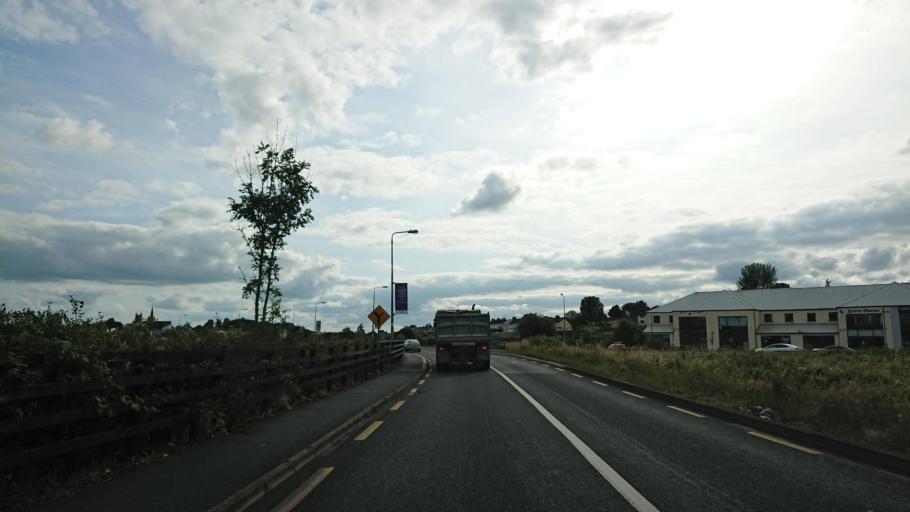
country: IE
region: Connaught
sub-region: County Leitrim
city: Carrick-on-Shannon
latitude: 53.9532
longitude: -8.0890
